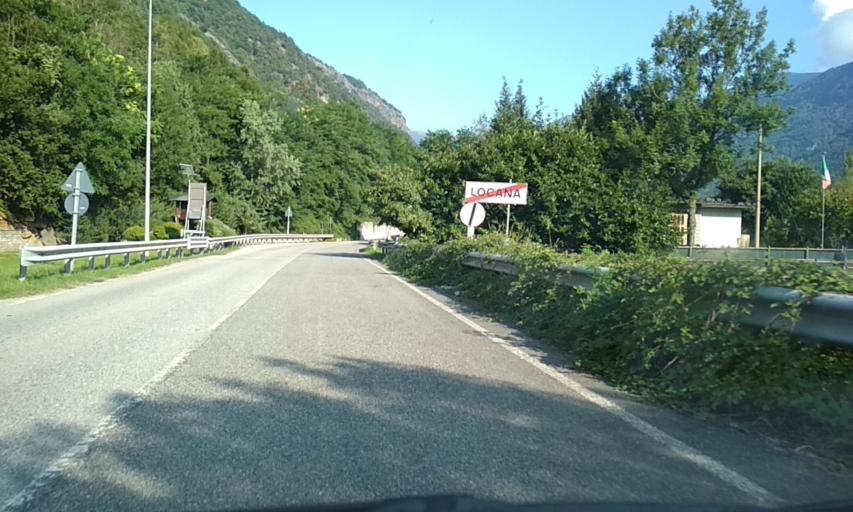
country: IT
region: Piedmont
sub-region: Provincia di Torino
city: Locana
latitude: 45.4162
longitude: 7.4663
